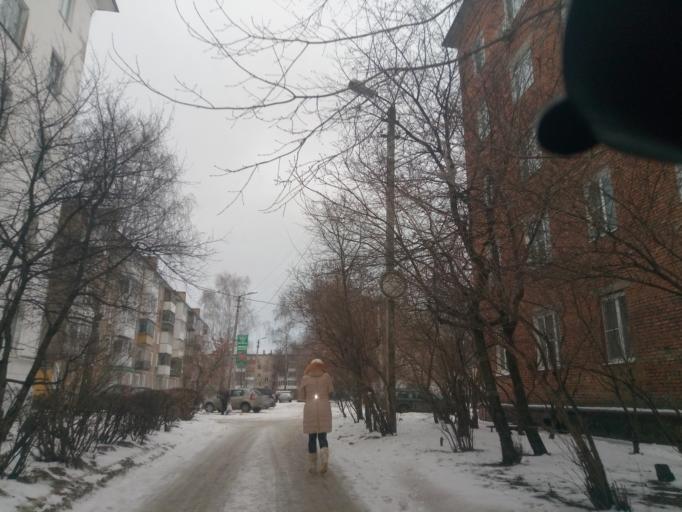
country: RU
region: Tula
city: Novomoskovsk
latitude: 54.0063
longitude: 38.2970
